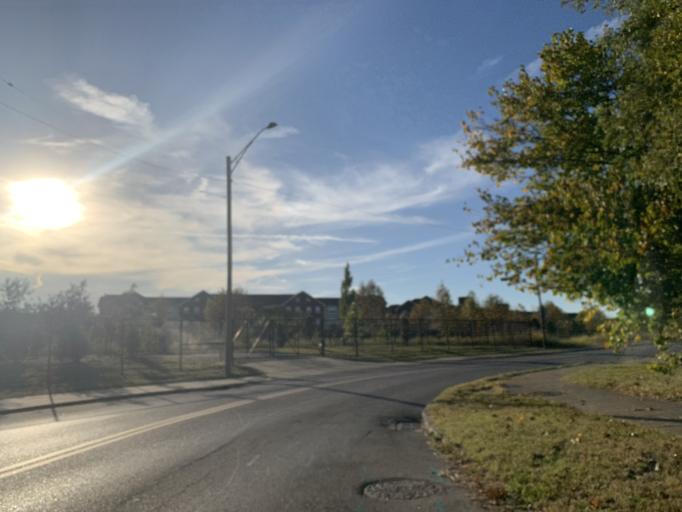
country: US
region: Kentucky
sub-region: Jefferson County
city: Louisville
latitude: 38.2238
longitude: -85.7654
